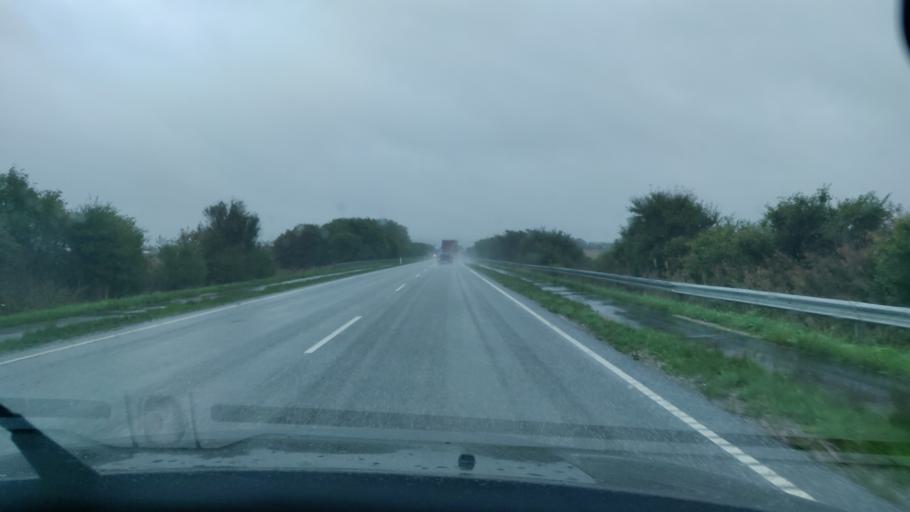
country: DK
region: North Denmark
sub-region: Thisted Kommune
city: Thisted
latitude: 56.8831
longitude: 8.6031
